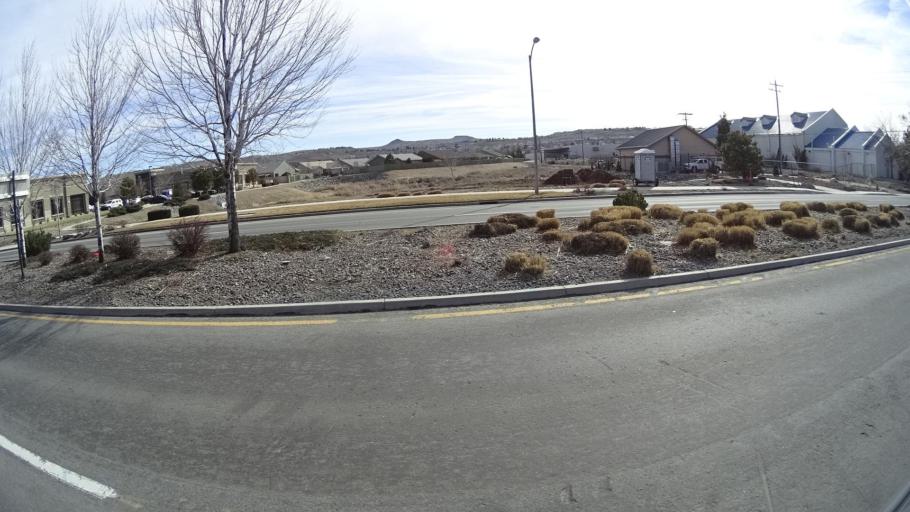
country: US
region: Nevada
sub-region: Washoe County
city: Sparks
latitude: 39.5785
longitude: -119.7242
